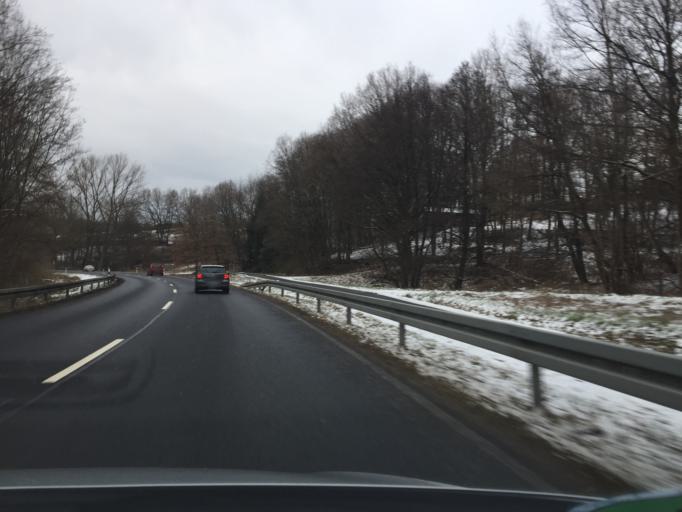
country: DE
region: Bavaria
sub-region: Regierungsbezirk Unterfranken
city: Mombris
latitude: 50.0505
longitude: 9.1952
